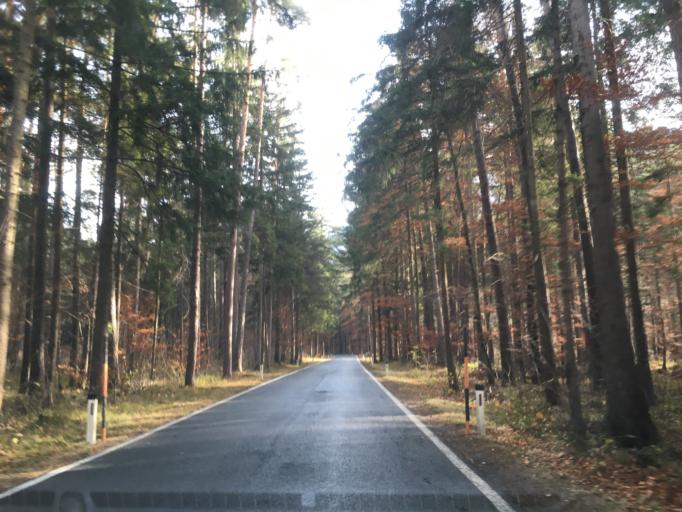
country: AT
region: Vorarlberg
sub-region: Politischer Bezirk Bludenz
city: Stallehr
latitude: 47.1389
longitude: 9.8436
